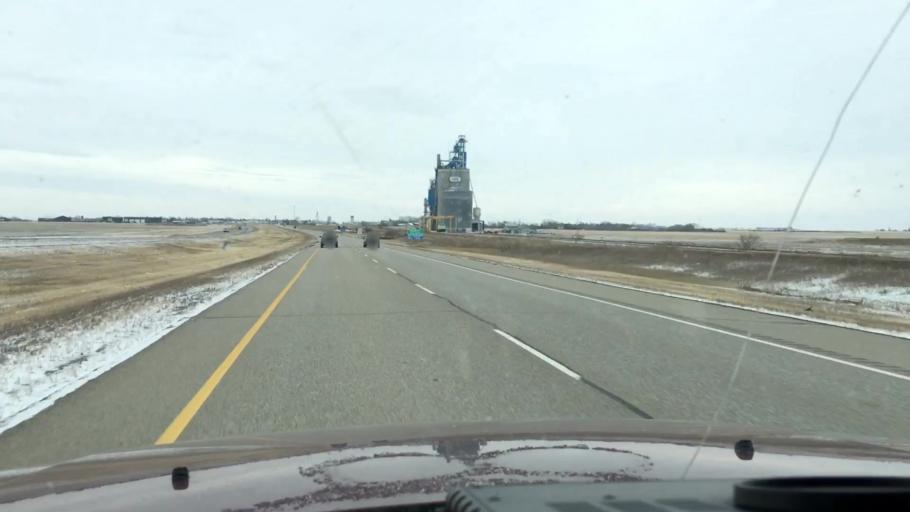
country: CA
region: Saskatchewan
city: Watrous
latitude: 51.2840
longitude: -106.0207
